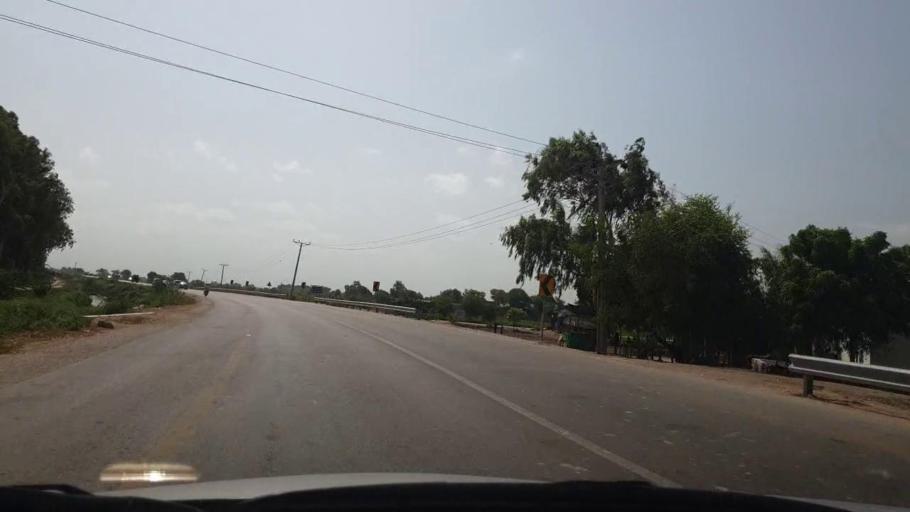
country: PK
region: Sindh
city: Matli
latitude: 24.9857
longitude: 68.6609
